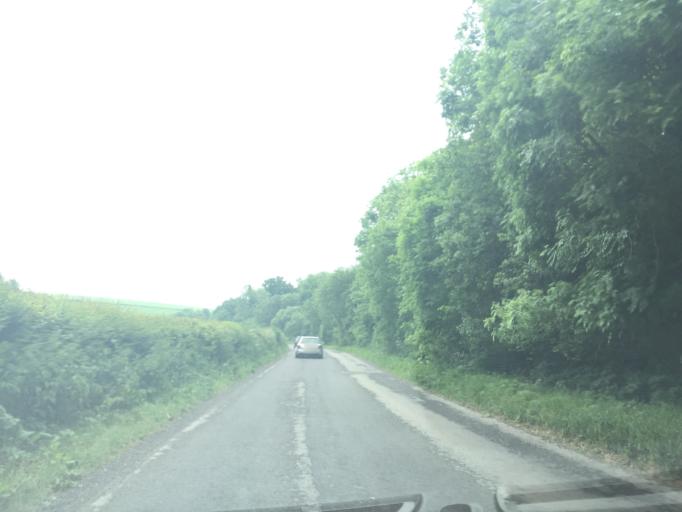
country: GB
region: England
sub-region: Dorset
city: Wool
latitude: 50.6466
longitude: -2.2675
